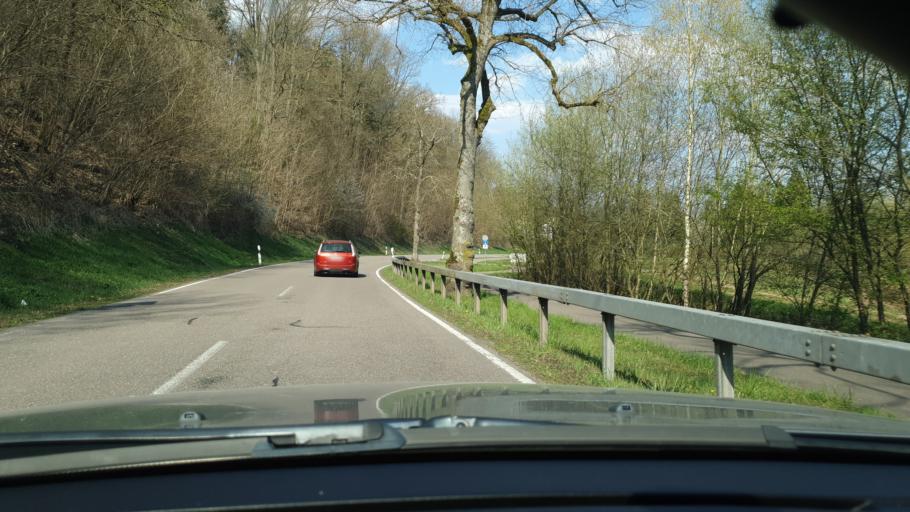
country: DE
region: Rheinland-Pfalz
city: Contwig
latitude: 49.2680
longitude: 7.4118
